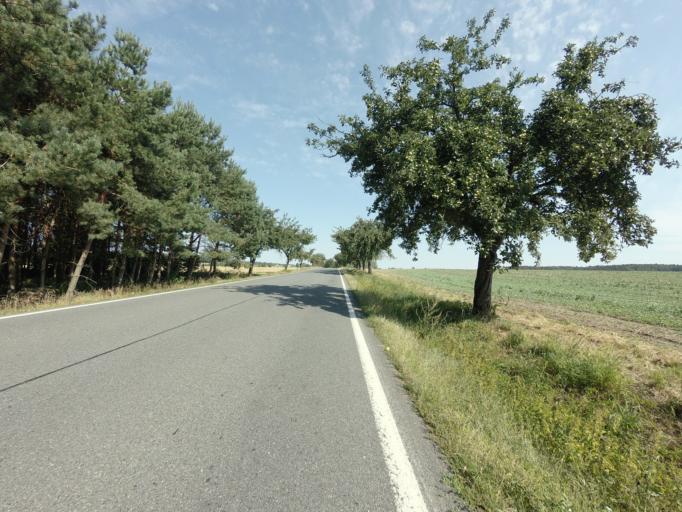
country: CZ
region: Jihocesky
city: Bernartice
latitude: 49.4004
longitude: 14.3632
